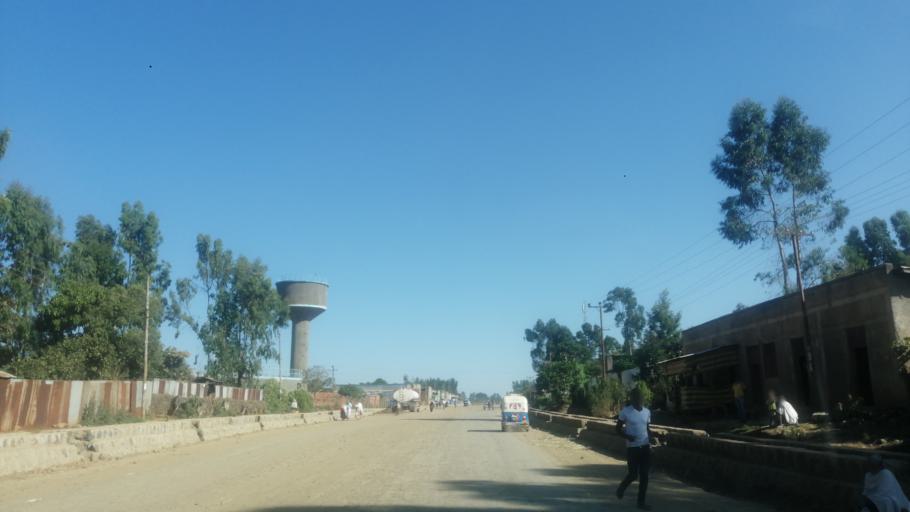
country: ET
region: Amhara
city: Addiet Canna
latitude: 11.0843
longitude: 37.8744
